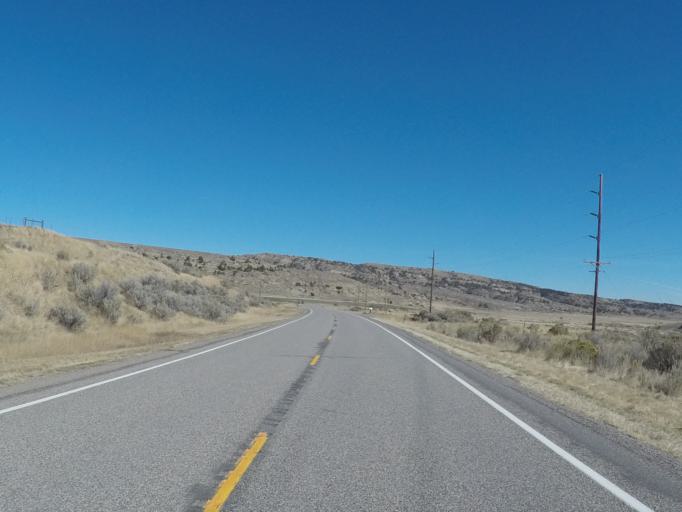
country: US
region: Montana
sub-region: Carbon County
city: Red Lodge
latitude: 45.1647
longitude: -109.1149
